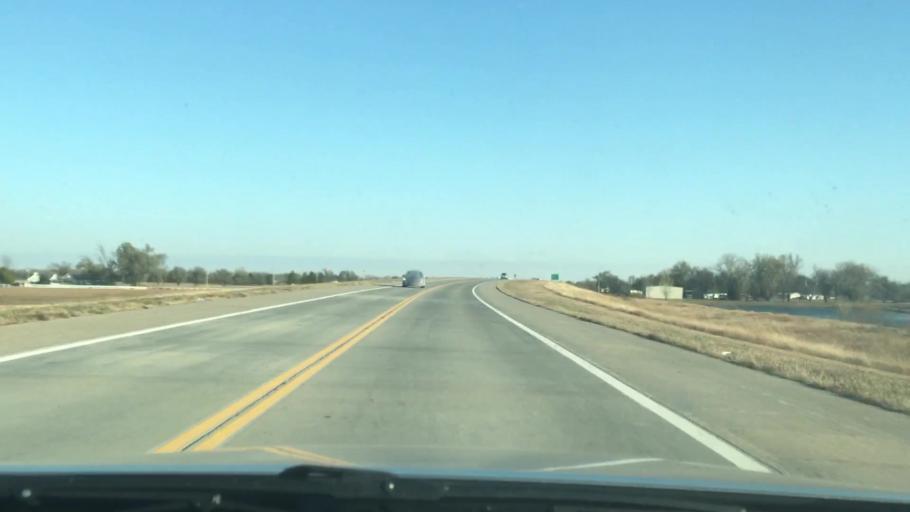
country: US
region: Kansas
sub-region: Reno County
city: Nickerson
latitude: 38.1042
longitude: -98.0189
